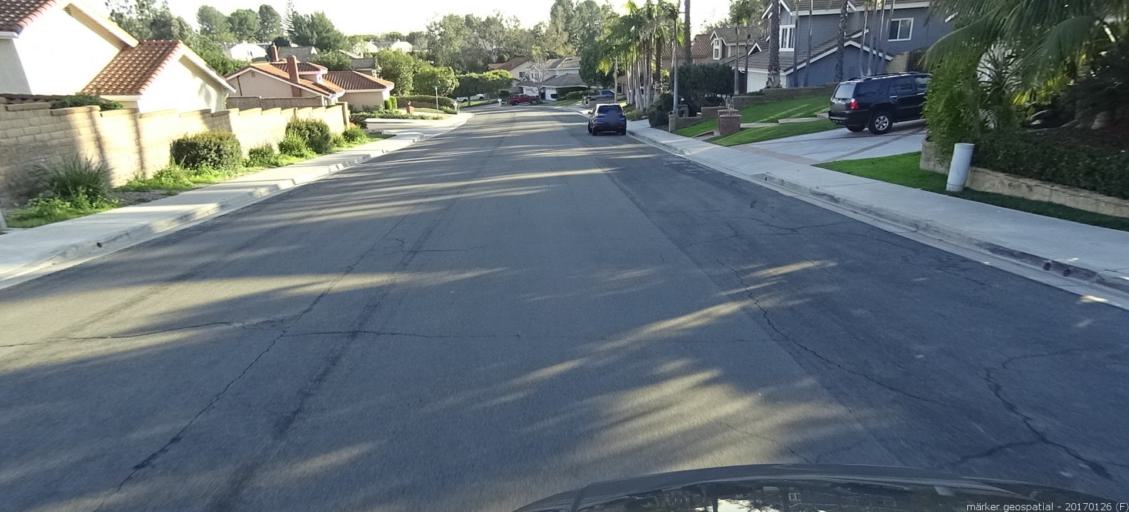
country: US
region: California
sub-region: Orange County
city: Lake Forest
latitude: 33.6439
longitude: -117.6730
